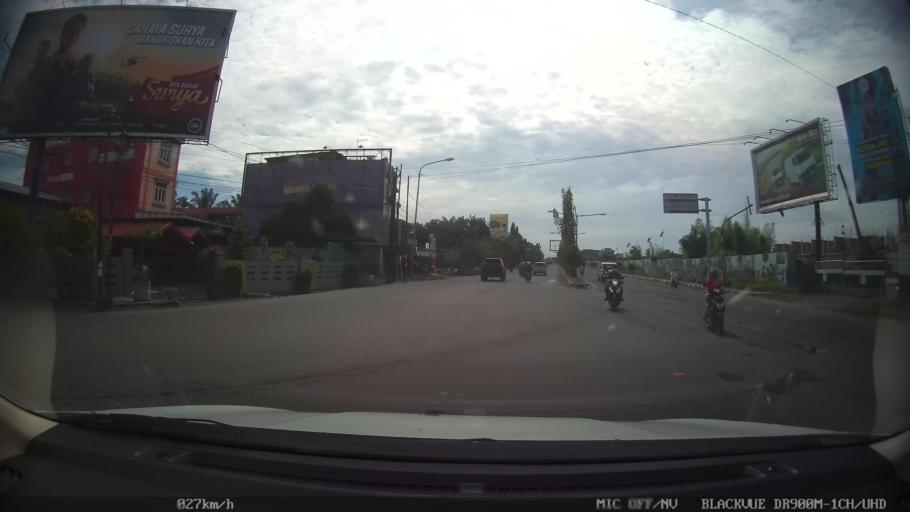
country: ID
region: North Sumatra
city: Medan
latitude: 3.6275
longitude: 98.6626
